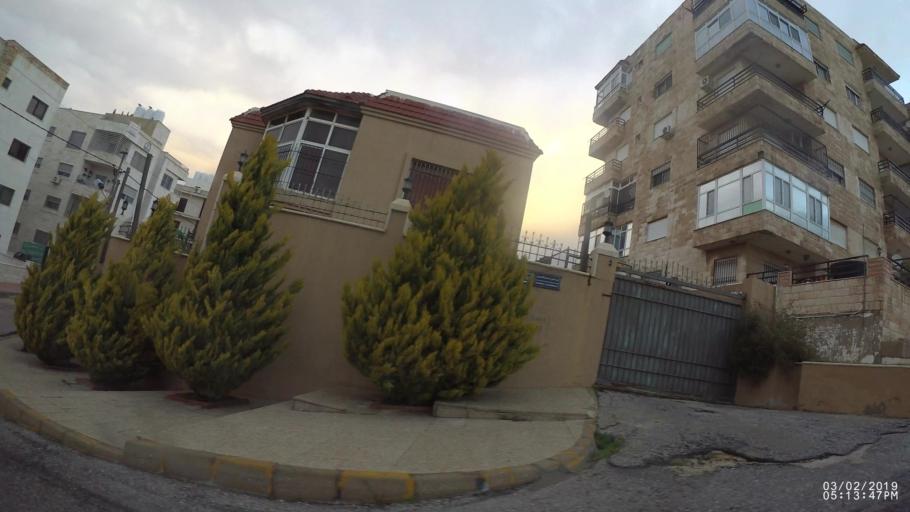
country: JO
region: Amman
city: Amman
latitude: 31.9874
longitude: 35.9130
